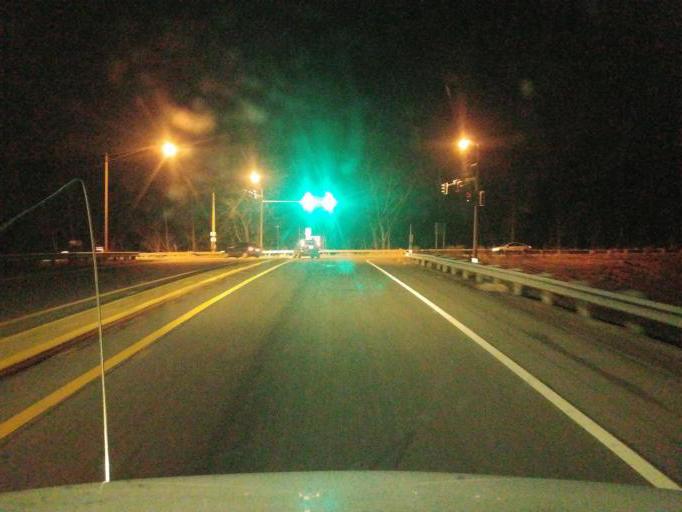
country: US
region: Ohio
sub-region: Tuscarawas County
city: Strasburg
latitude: 40.5827
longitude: -81.5202
